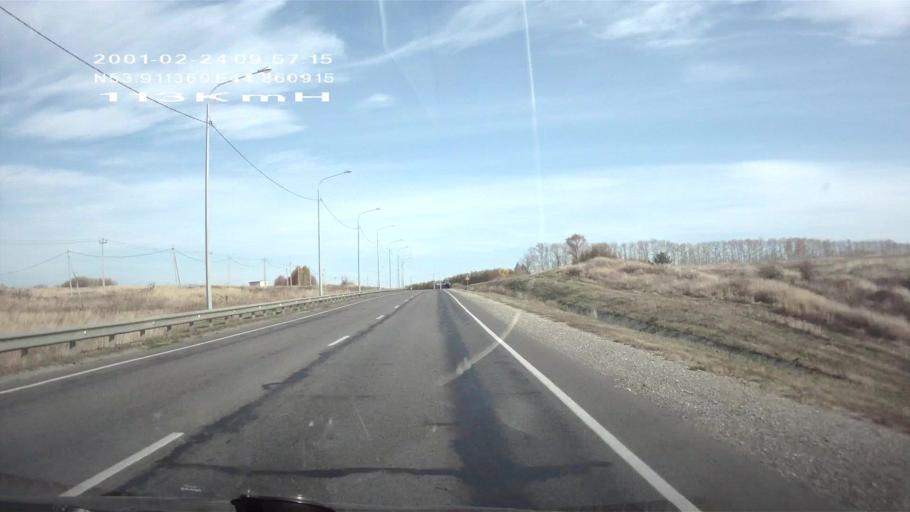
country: RU
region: Penza
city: Issa
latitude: 53.9113
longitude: 44.8613
